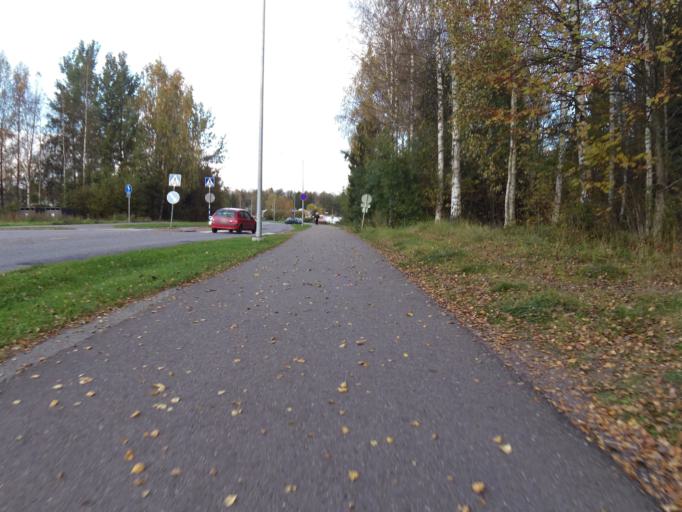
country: FI
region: Uusimaa
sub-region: Helsinki
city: Kauniainen
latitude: 60.3022
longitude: 24.7391
